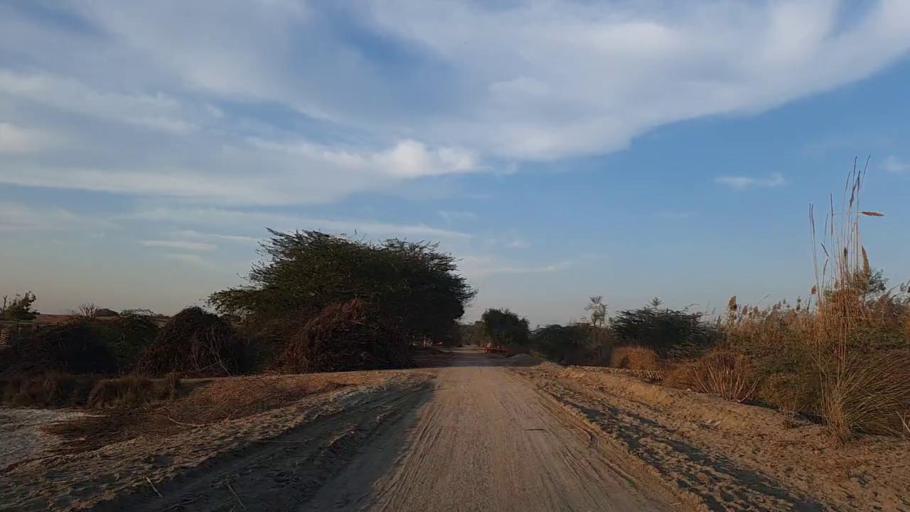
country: PK
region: Sindh
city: Bandhi
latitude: 26.6069
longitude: 68.3592
